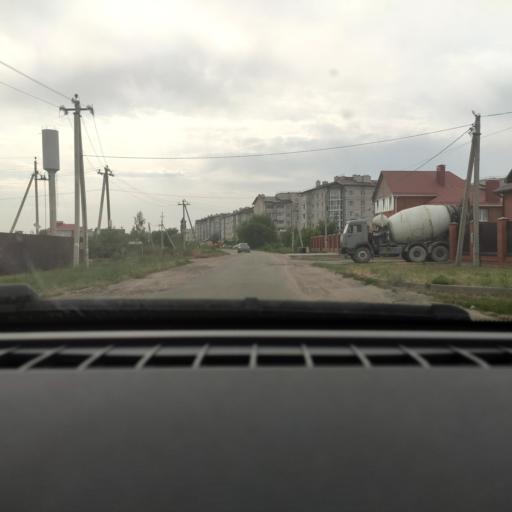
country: RU
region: Voronezj
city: Novaya Usman'
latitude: 51.6498
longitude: 39.3383
